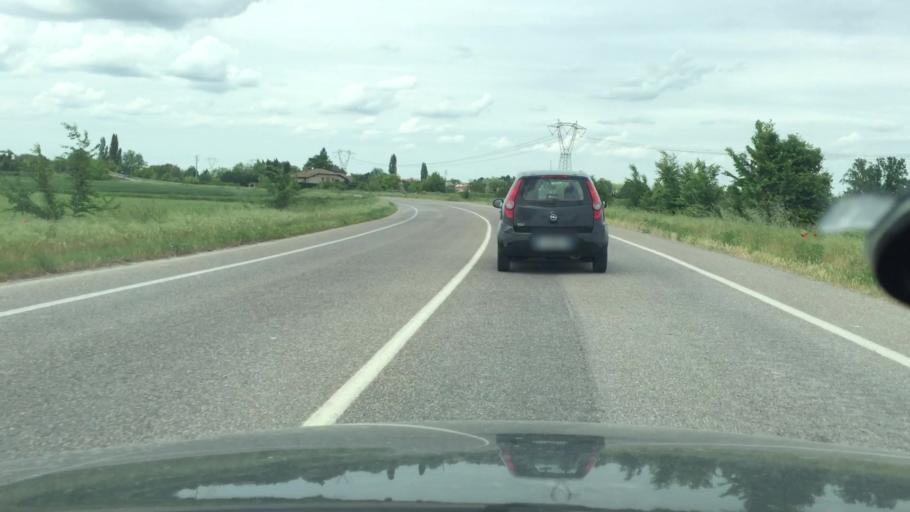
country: IT
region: Emilia-Romagna
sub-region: Provincia di Ferrara
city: Cona
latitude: 44.8084
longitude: 11.7185
